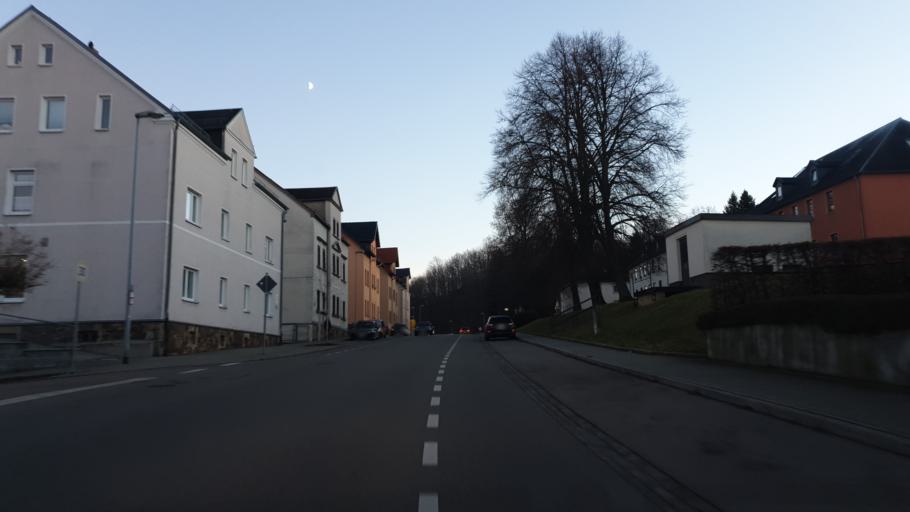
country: DE
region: Saxony
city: Hohndorf
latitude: 50.7393
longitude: 12.6818
